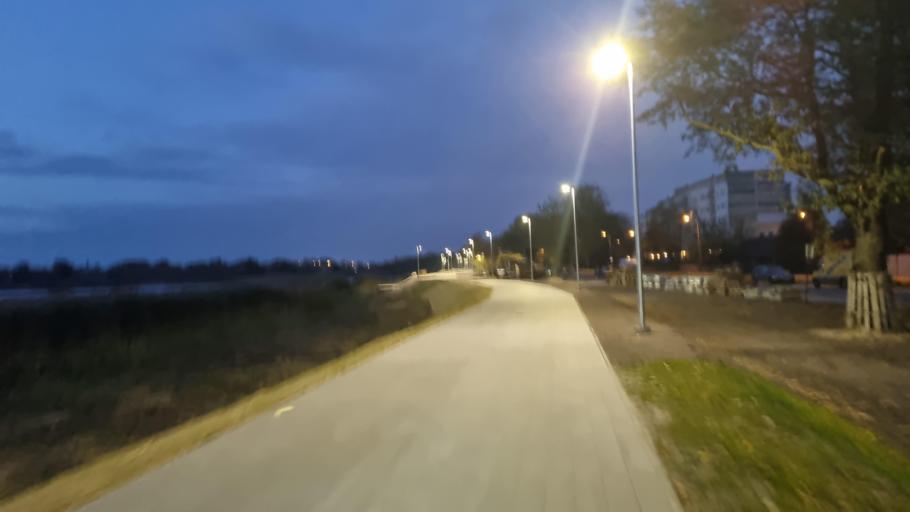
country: LV
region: Riga
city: Daugavgriva
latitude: 57.0306
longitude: 24.0324
